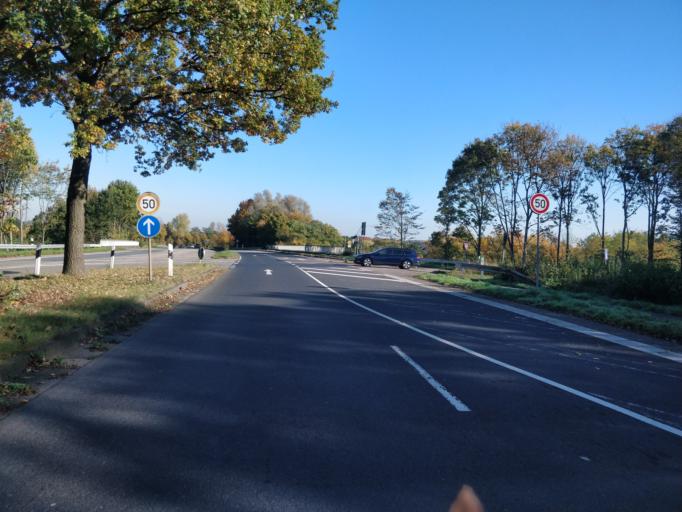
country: DE
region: North Rhine-Westphalia
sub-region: Regierungsbezirk Koln
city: Sinnersdorf
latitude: 51.0409
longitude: 6.8388
